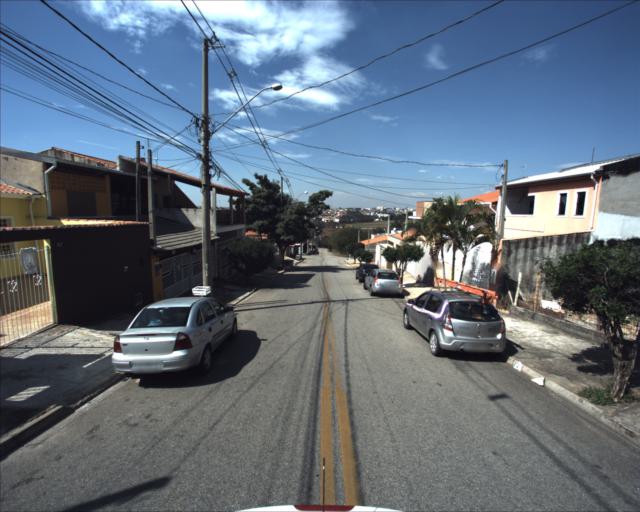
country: BR
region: Sao Paulo
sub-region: Sorocaba
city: Sorocaba
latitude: -23.4847
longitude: -47.5095
